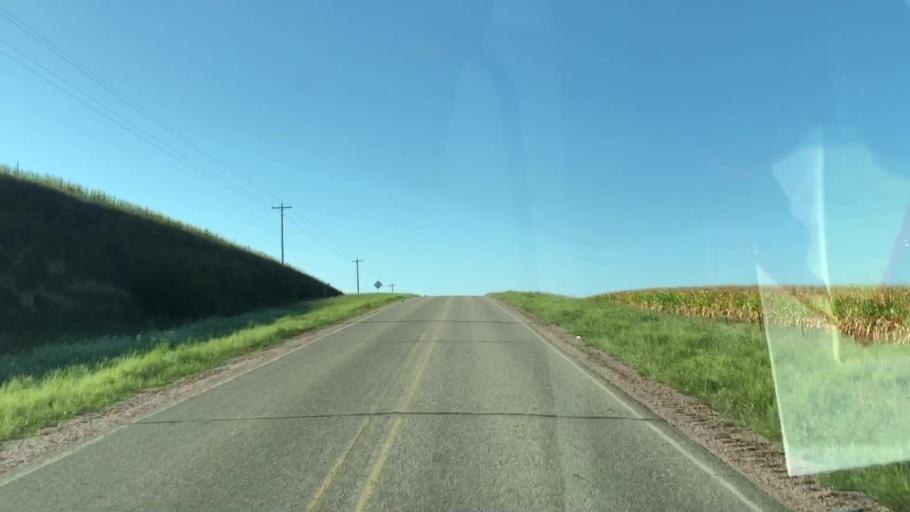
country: US
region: Iowa
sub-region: Woodbury County
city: Moville
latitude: 42.4737
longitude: -96.2136
